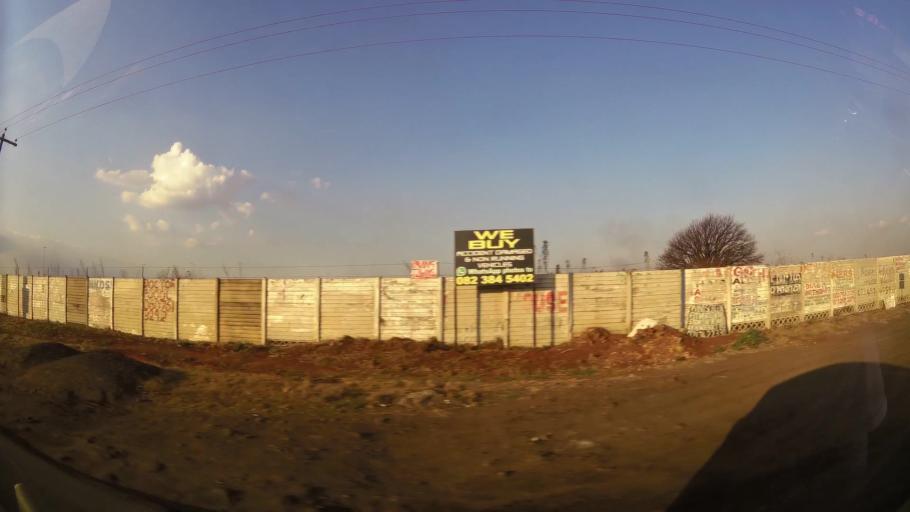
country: ZA
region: Gauteng
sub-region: Ekurhuleni Metropolitan Municipality
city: Germiston
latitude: -26.2910
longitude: 28.2298
